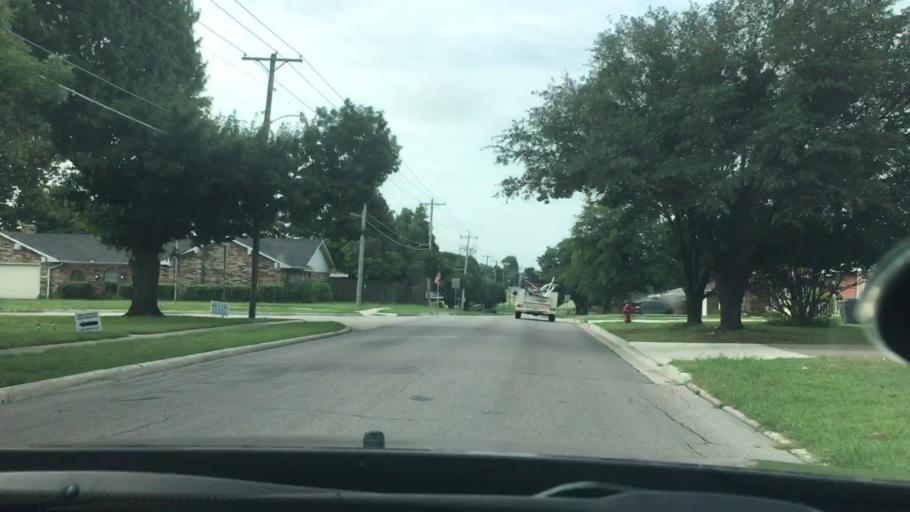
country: US
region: Oklahoma
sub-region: Carter County
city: Ardmore
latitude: 34.1937
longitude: -97.1255
